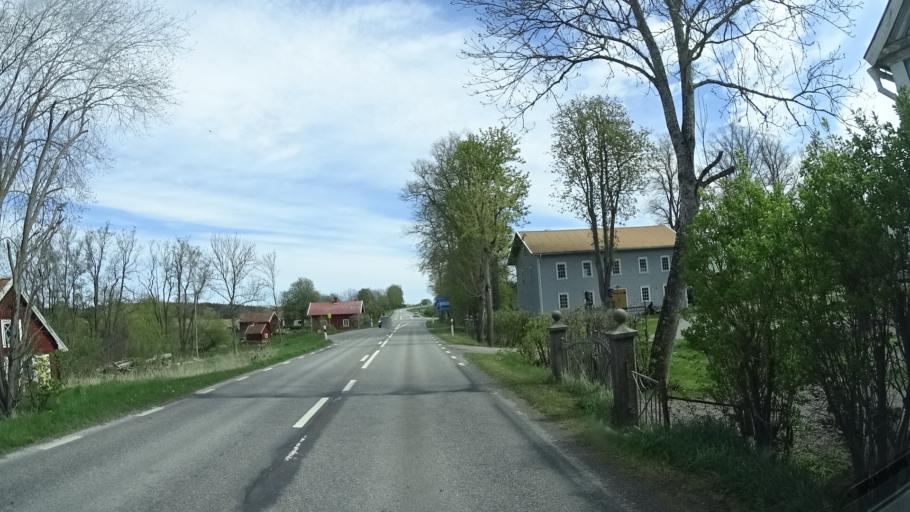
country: SE
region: OEstergoetland
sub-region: Linkopings Kommun
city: Vikingstad
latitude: 58.3707
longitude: 15.3744
